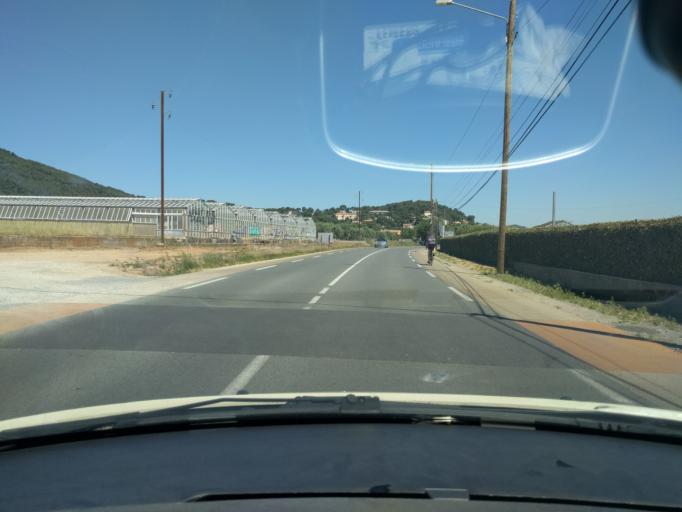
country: FR
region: Provence-Alpes-Cote d'Azur
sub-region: Departement du Var
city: Hyeres
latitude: 43.0862
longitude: 6.1289
